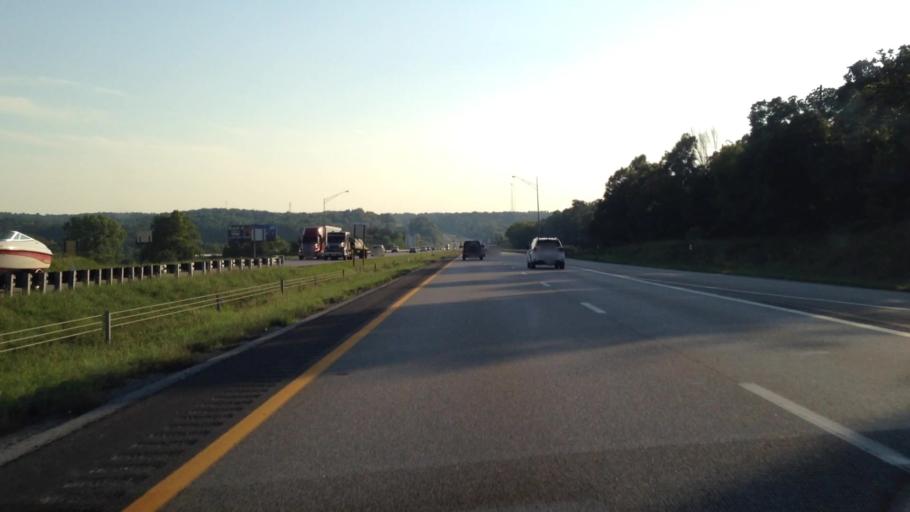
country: US
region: Missouri
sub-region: Jasper County
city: Joplin
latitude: 37.0357
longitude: -94.5160
